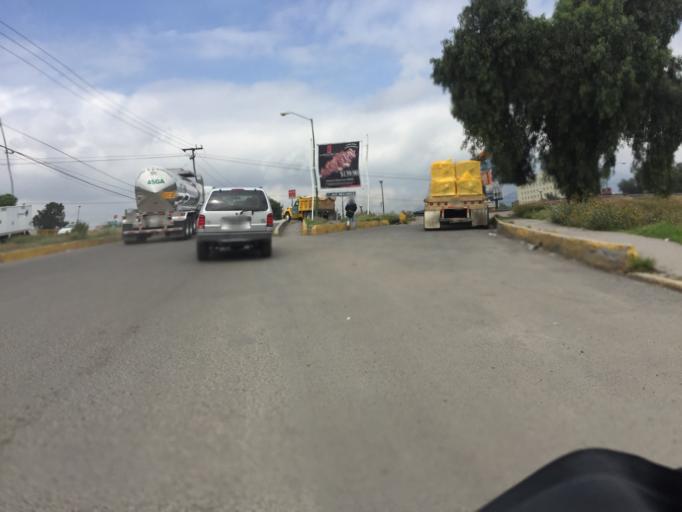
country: MX
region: Mexico
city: Cuautitlan
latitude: 19.6694
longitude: -99.1988
